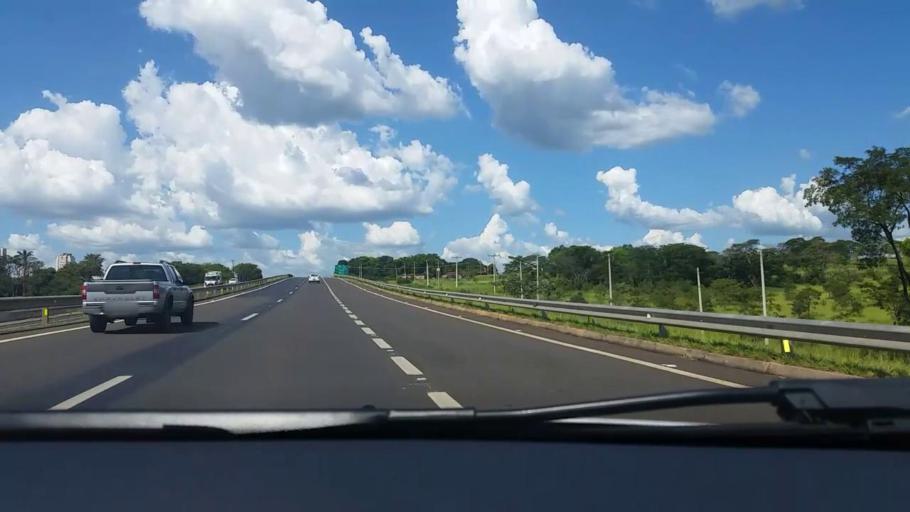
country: BR
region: Sao Paulo
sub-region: Bauru
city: Bauru
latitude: -22.3840
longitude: -49.0690
